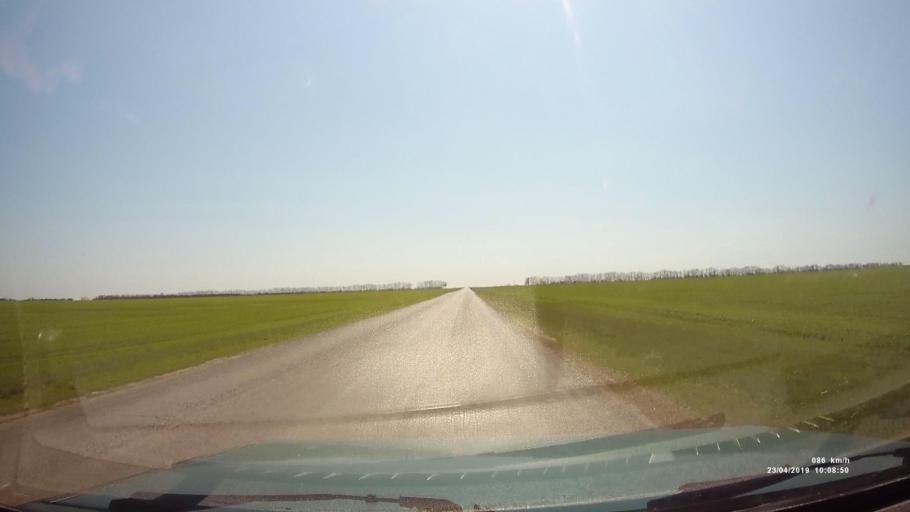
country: RU
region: Rostov
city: Sovetskoye
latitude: 46.7160
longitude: 42.2722
